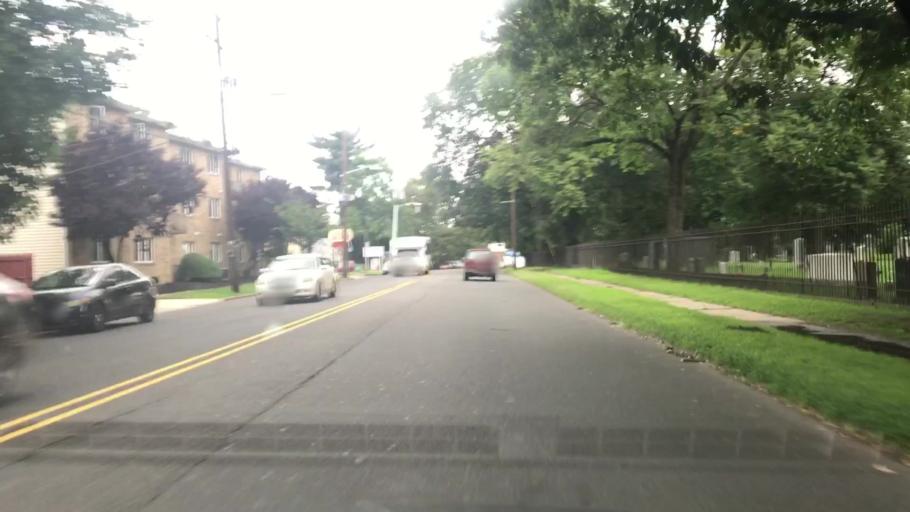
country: US
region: New Jersey
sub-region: Union County
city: Hillside
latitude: 40.6925
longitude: -74.2157
